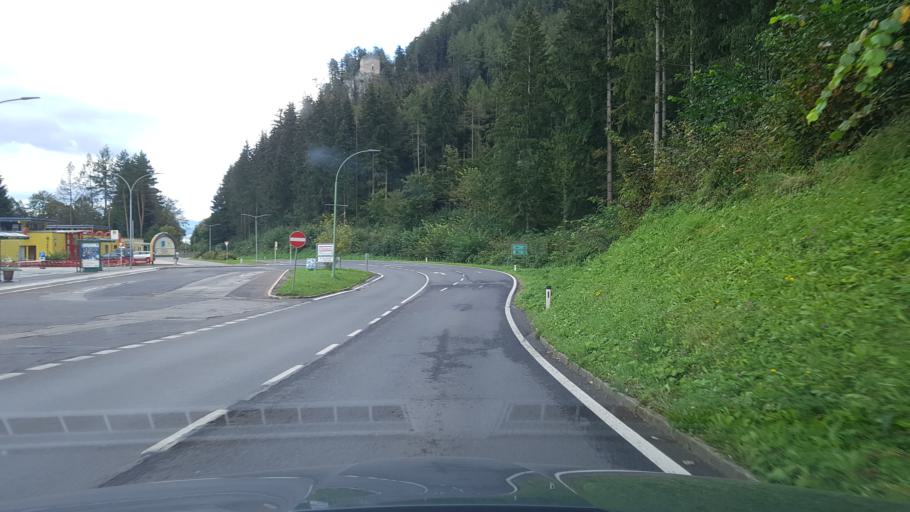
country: AT
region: Styria
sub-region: Politischer Bezirk Murtal
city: Judenburg
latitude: 47.1670
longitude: 14.6695
